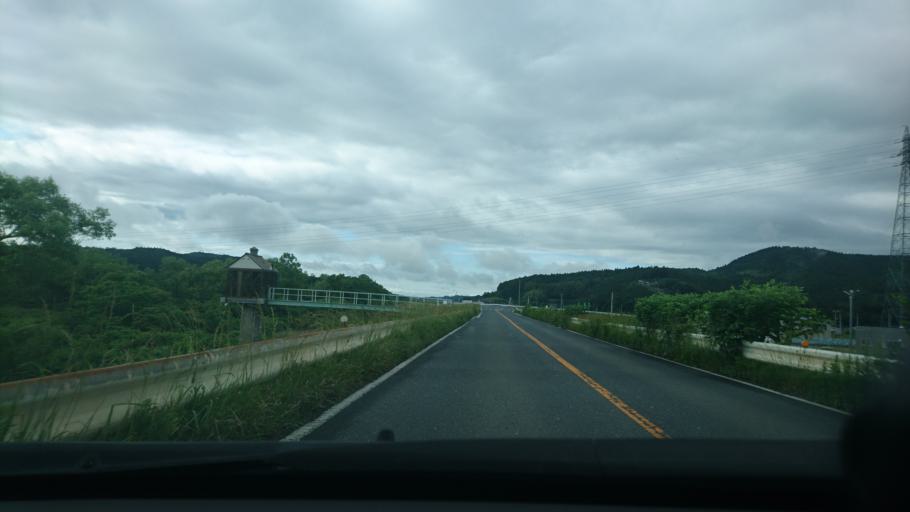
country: JP
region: Miyagi
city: Wakuya
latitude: 38.6169
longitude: 141.2988
